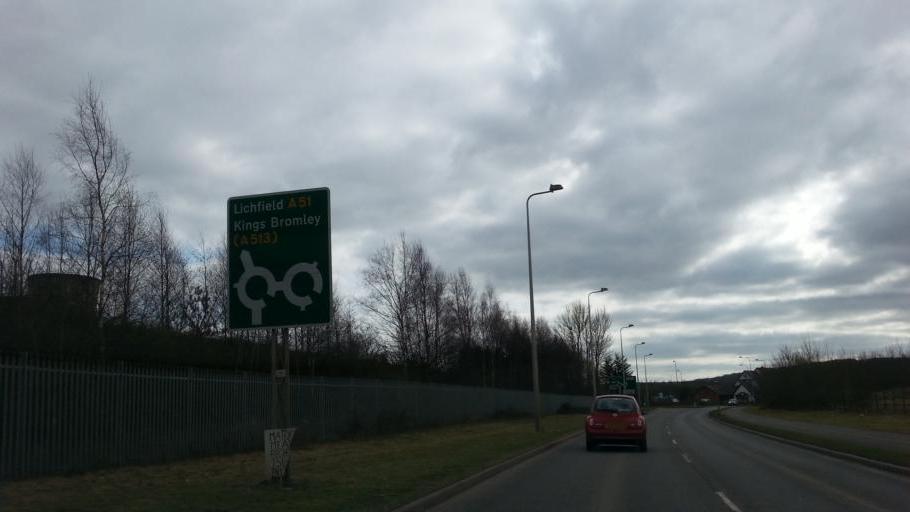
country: GB
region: England
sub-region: Staffordshire
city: Rugeley
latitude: 52.7599
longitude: -1.9252
